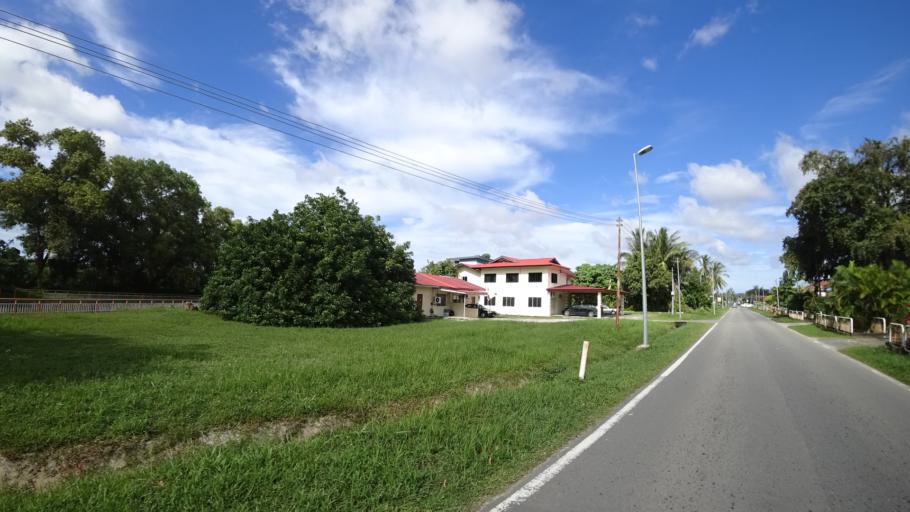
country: BN
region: Brunei and Muara
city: Bandar Seri Begawan
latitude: 4.9366
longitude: 114.9450
